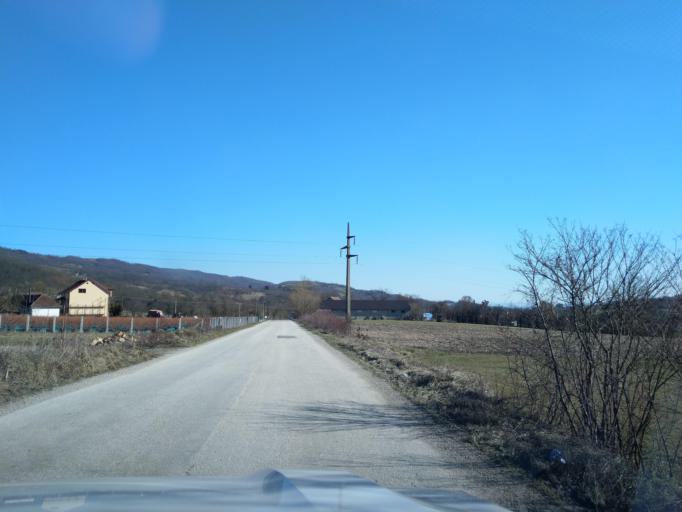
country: RS
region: Central Serbia
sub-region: Zlatiborski Okrug
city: Kosjeric
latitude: 43.9304
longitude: 19.8949
